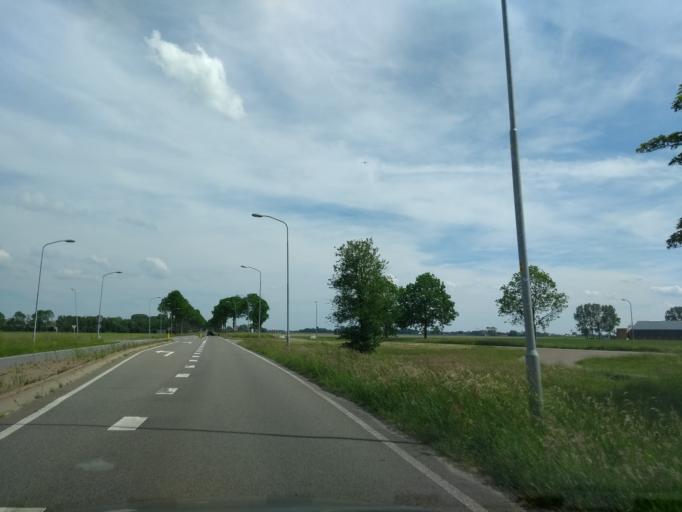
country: NL
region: Groningen
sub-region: Gemeente Zuidhorn
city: Oldehove
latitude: 53.3618
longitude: 6.4037
